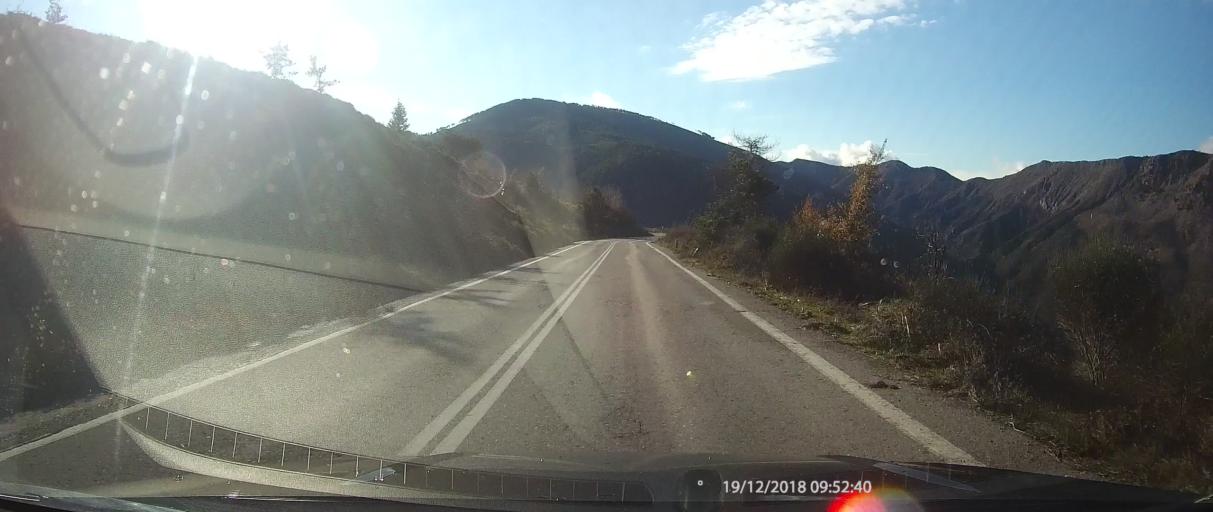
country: GR
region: Peloponnese
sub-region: Nomos Messinias
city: Paralia Vergas
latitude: 37.0724
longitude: 22.2548
